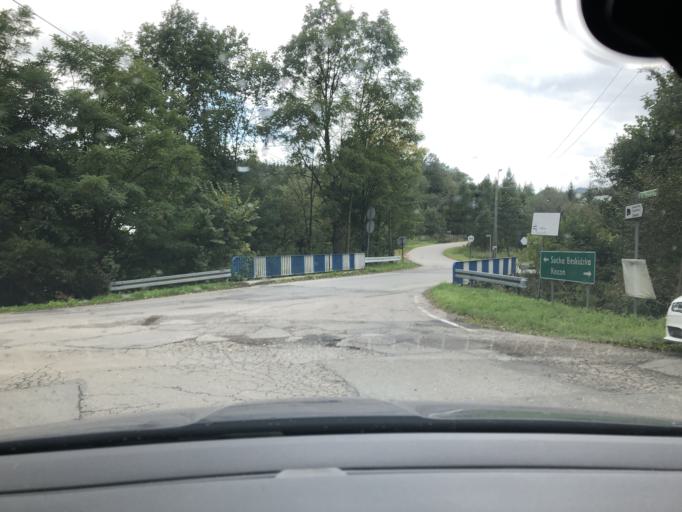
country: PL
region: Silesian Voivodeship
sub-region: Powiat zywiecki
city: Slemien
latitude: 49.7231
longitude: 19.3773
